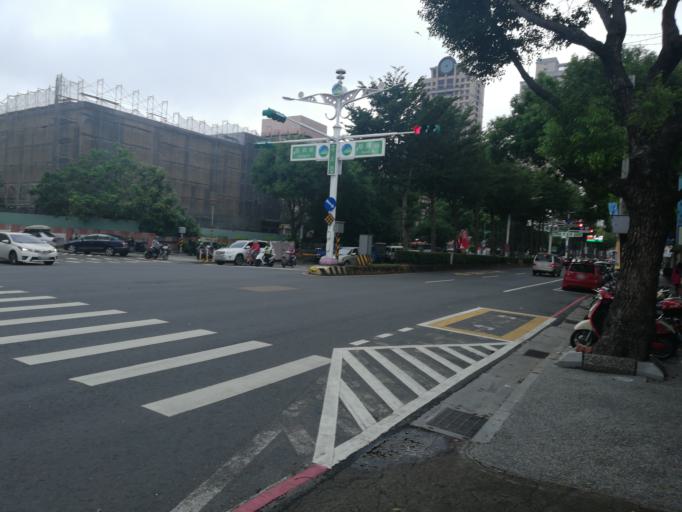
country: TW
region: Taiwan
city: Taoyuan City
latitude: 25.0086
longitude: 121.3025
